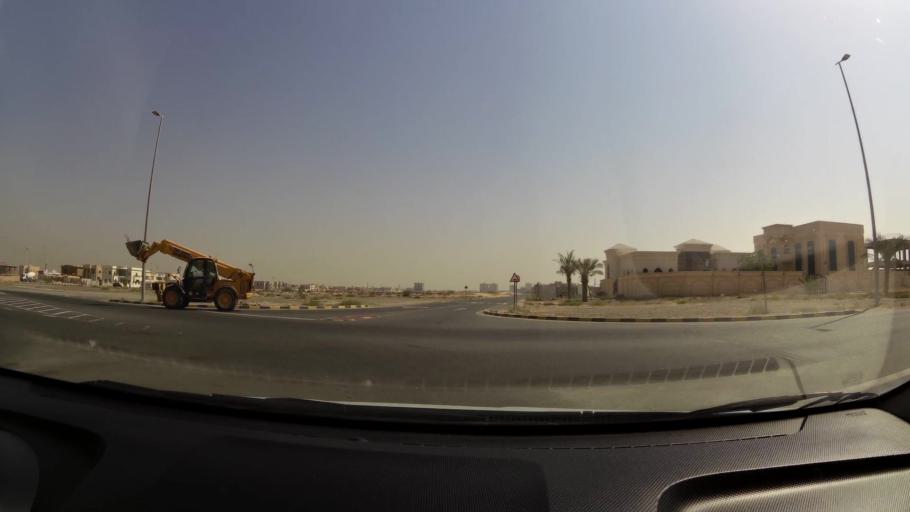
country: AE
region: Ajman
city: Ajman
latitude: 25.4125
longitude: 55.5287
